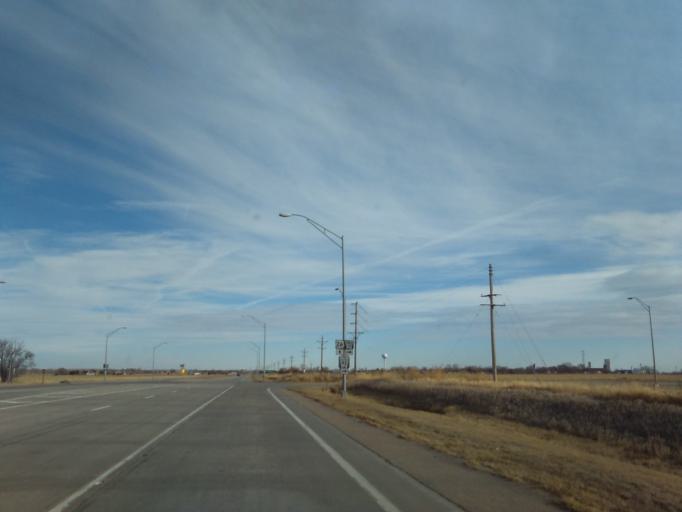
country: US
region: Nebraska
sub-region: Scotts Bluff County
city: Gering
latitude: 41.8148
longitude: -103.5210
